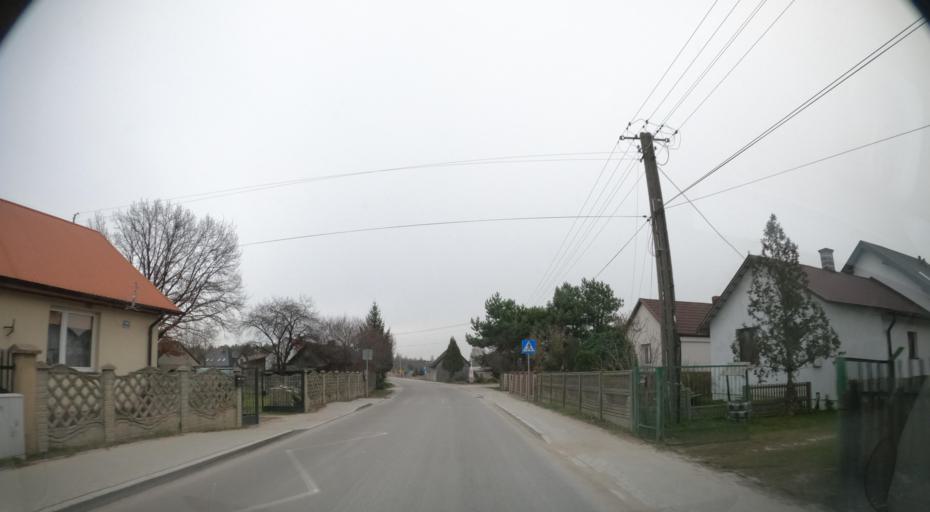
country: PL
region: Masovian Voivodeship
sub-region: Powiat radomski
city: Jastrzebia
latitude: 51.4892
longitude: 21.1869
